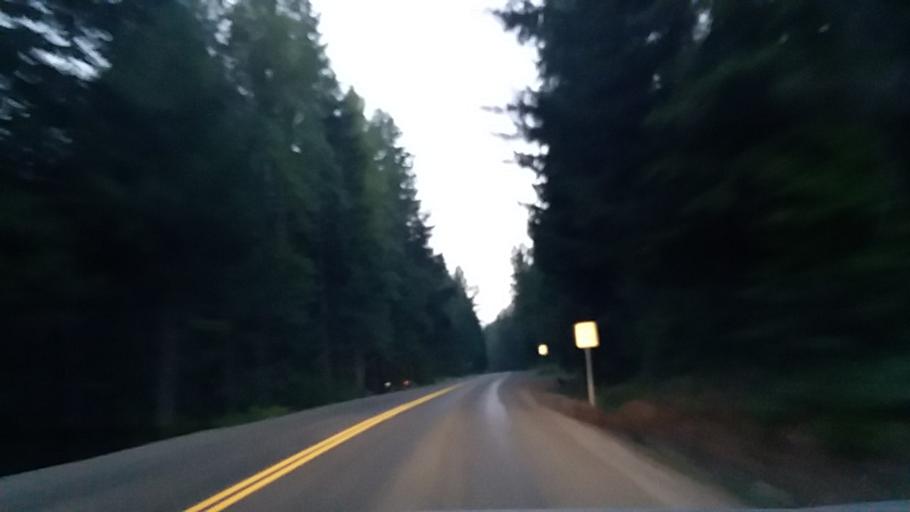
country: US
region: Washington
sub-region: Kittitas County
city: Cle Elum
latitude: 47.3284
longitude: -121.2662
